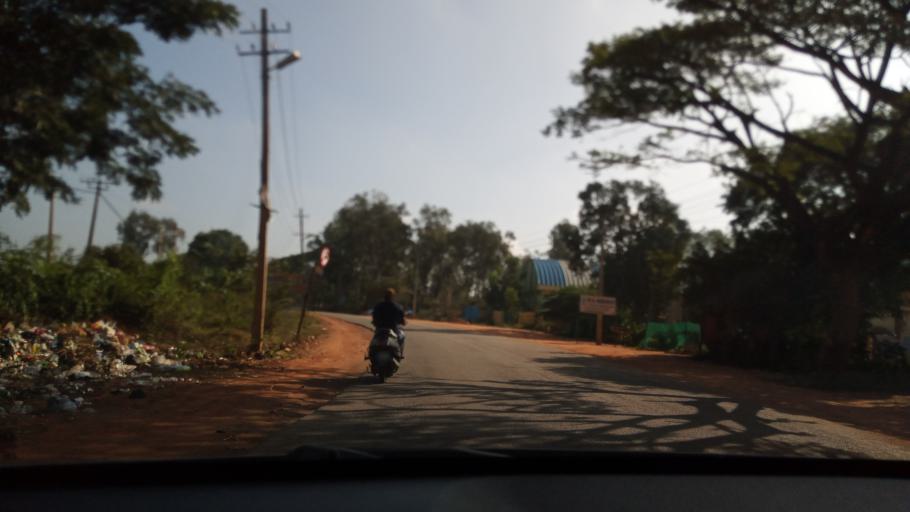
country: IN
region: Karnataka
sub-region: Bangalore Rural
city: Devanhalli
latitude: 13.2569
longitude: 77.7253
